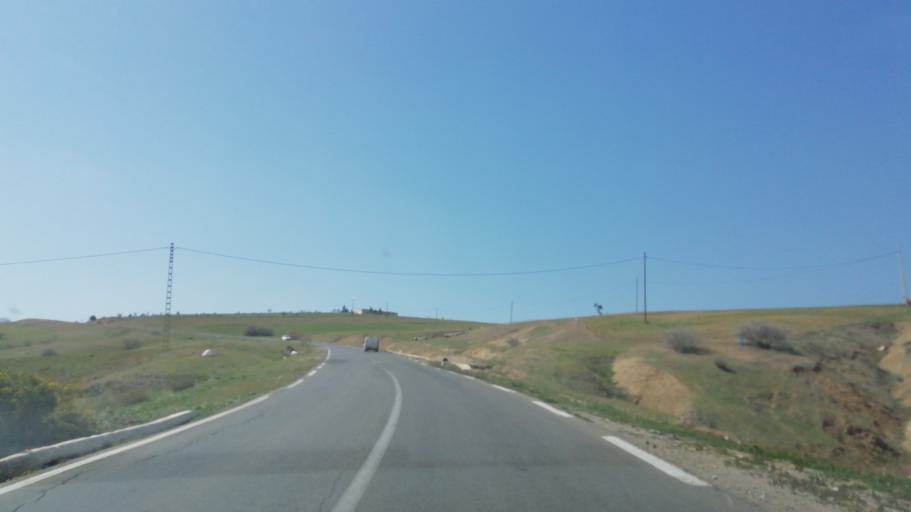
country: DZ
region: Mascara
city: Mascara
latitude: 35.5440
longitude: 0.1098
